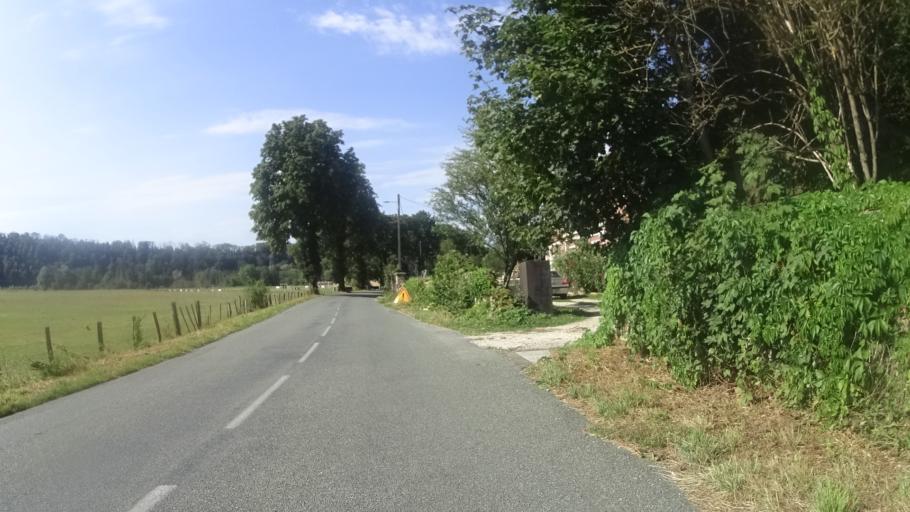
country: FR
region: Franche-Comte
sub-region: Departement du Doubs
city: Clerval
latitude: 47.4444
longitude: 6.5720
